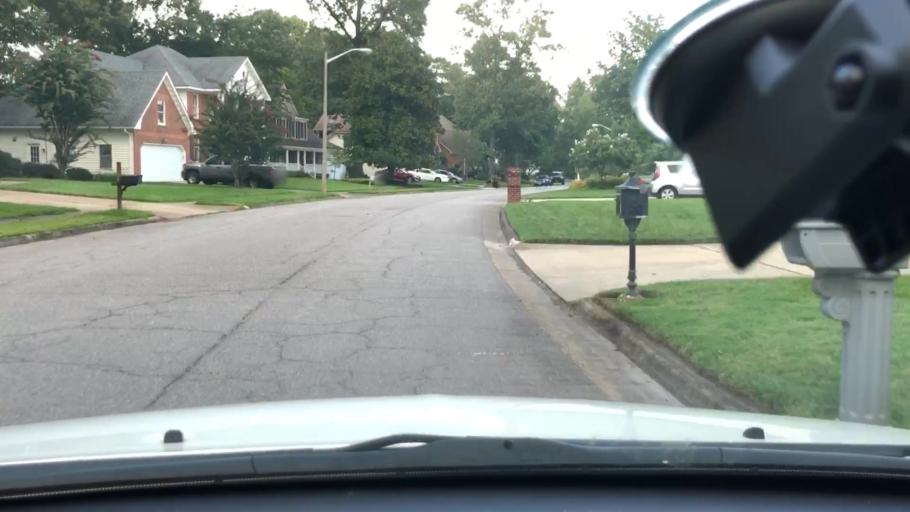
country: US
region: Virginia
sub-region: City of Chesapeake
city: Chesapeake
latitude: 36.7040
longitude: -76.2883
